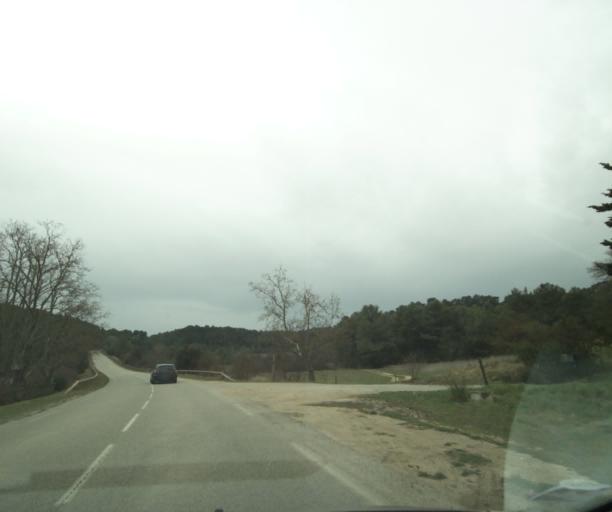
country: FR
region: Provence-Alpes-Cote d'Azur
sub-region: Departement des Bouches-du-Rhone
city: Saint-Marc-Jaumegarde
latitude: 43.5560
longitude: 5.5457
